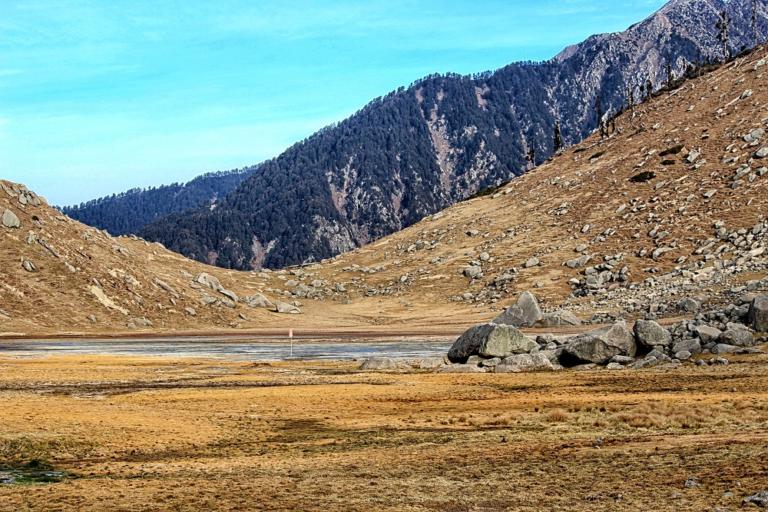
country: IN
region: Himachal Pradesh
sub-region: Kangra
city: Dharmsala
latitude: 32.3239
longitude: 76.2753
